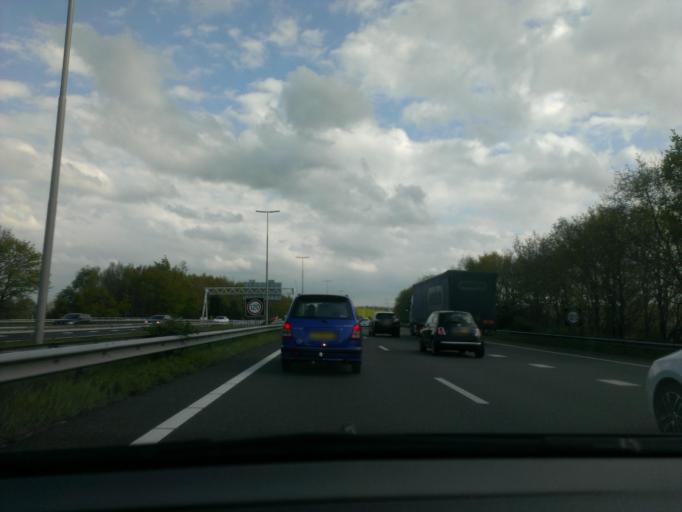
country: NL
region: Gelderland
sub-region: Gemeente Hattem
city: Hattem
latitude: 52.4794
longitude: 6.0328
